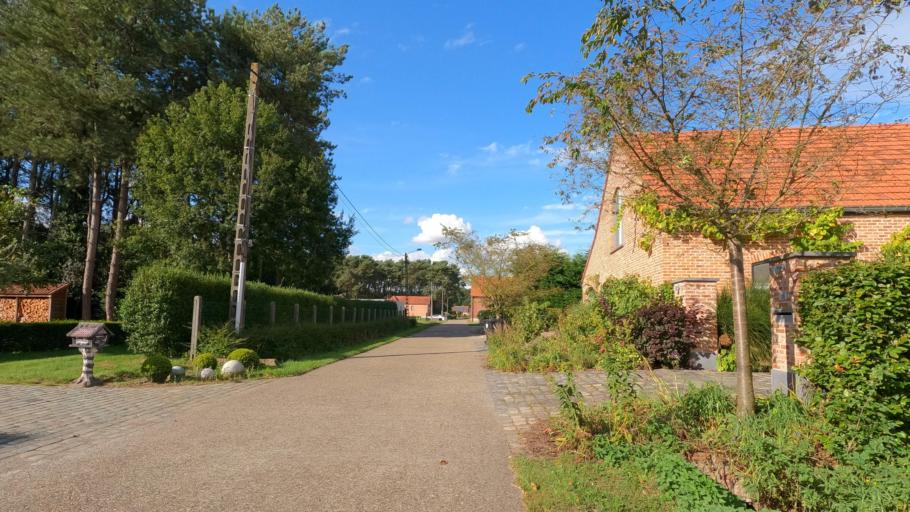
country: BE
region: Flanders
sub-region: Provincie Antwerpen
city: Herselt
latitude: 51.0410
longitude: 4.8821
